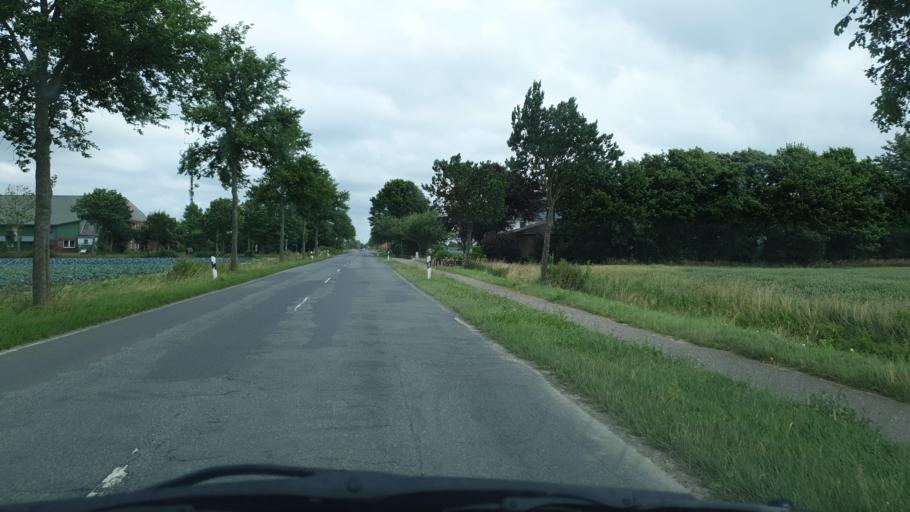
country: DE
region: Schleswig-Holstein
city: Friedrichskoog
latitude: 54.0189
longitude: 8.8845
